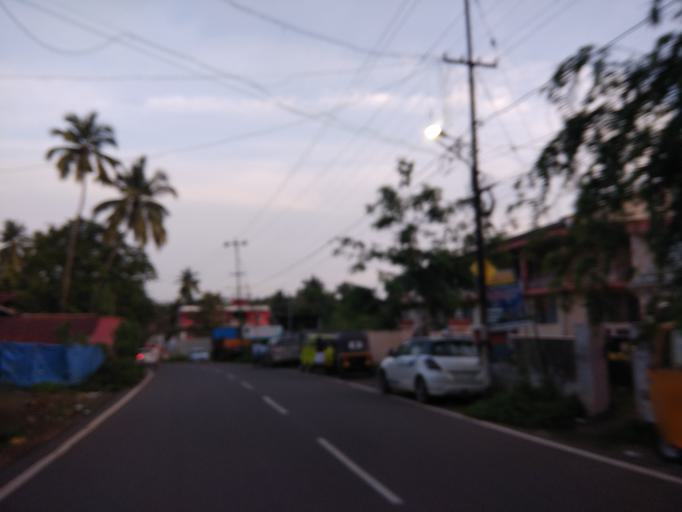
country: IN
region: Kerala
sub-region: Thrissur District
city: Trichur
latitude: 10.5203
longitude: 76.2023
